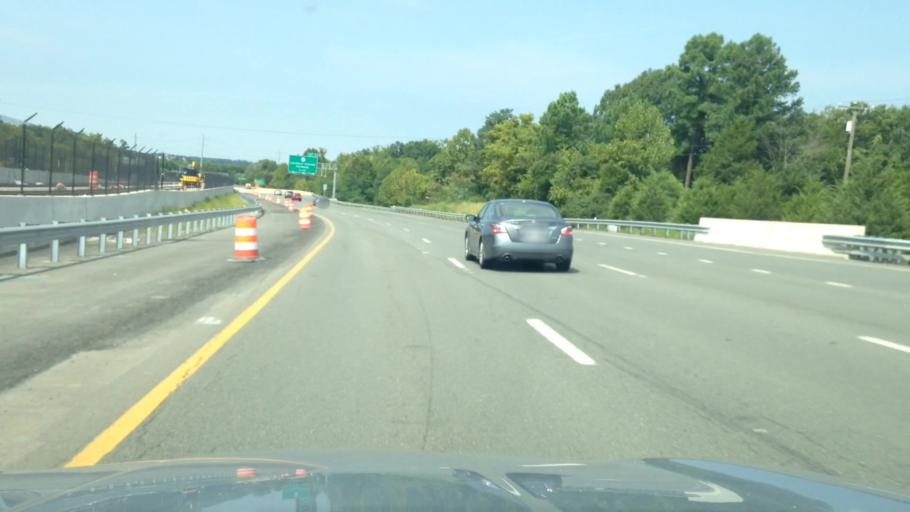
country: US
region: Virginia
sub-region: Loudoun County
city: Sterling
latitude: 38.9934
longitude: -77.4630
